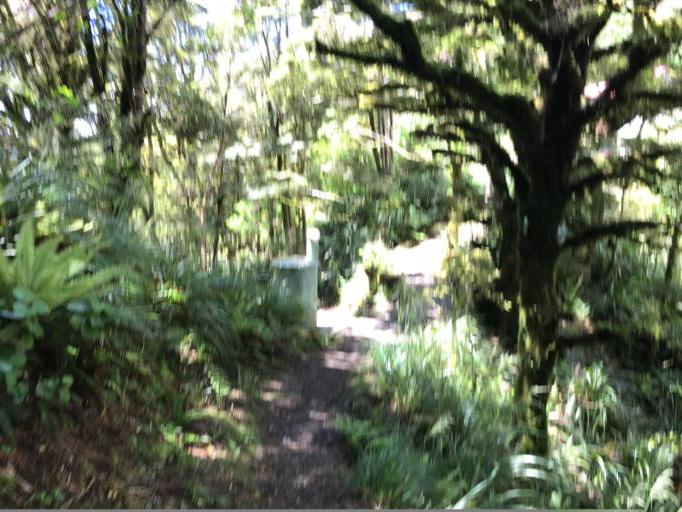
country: NZ
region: Wellington
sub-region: Kapiti Coast District
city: Otaki
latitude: -40.9075
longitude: 175.2559
